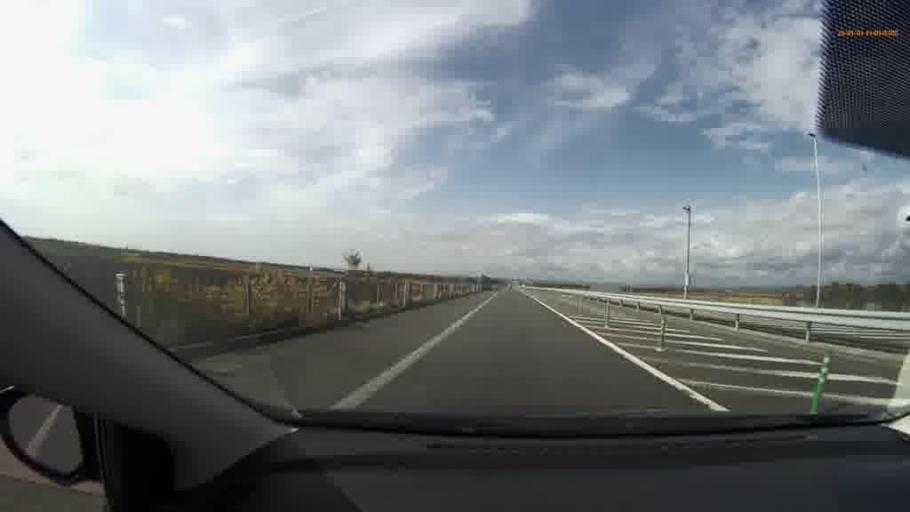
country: JP
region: Hokkaido
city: Kushiro
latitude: 43.0370
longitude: 144.3499
